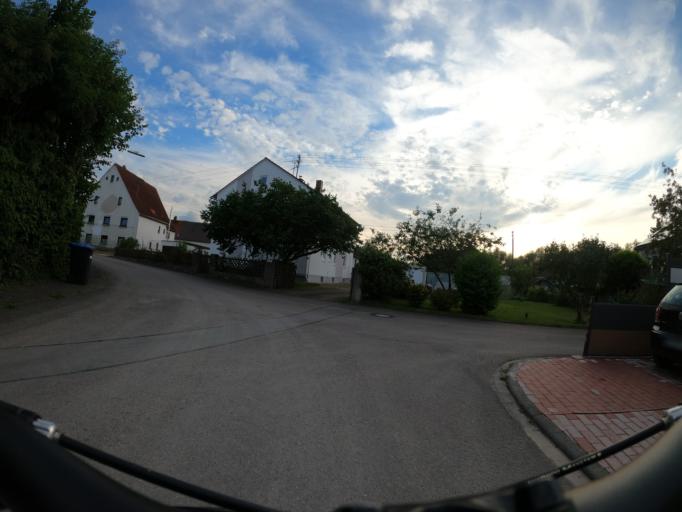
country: DE
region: Bavaria
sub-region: Swabia
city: Nersingen
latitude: 48.4313
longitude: 10.1439
